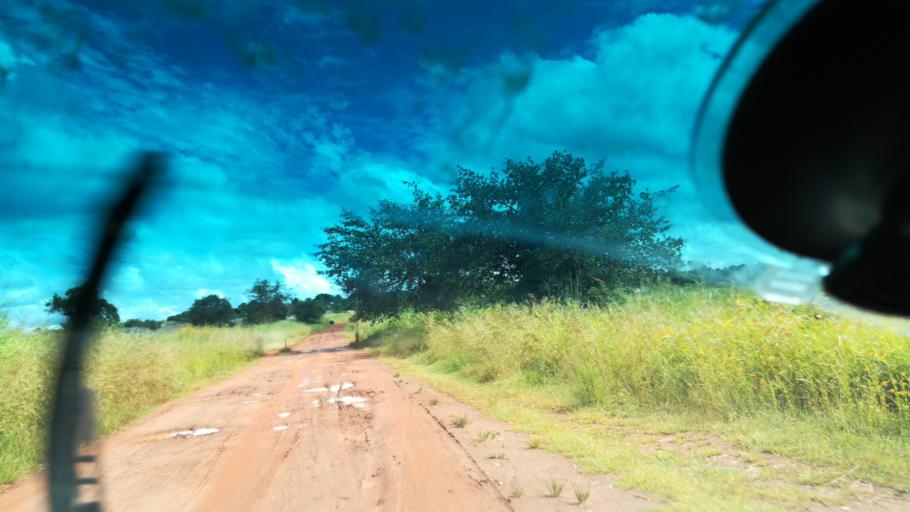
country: ZM
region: Luapula
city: Nchelenge
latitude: -9.1071
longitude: 28.3018
